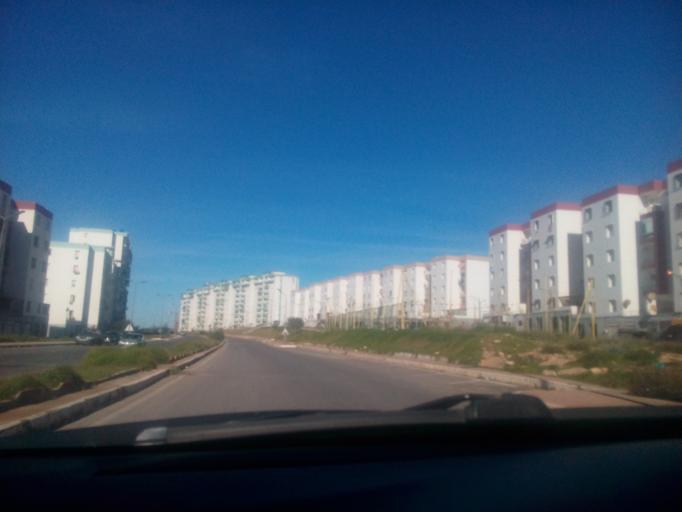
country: DZ
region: Oran
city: Bir el Djir
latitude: 35.7516
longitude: -0.5532
